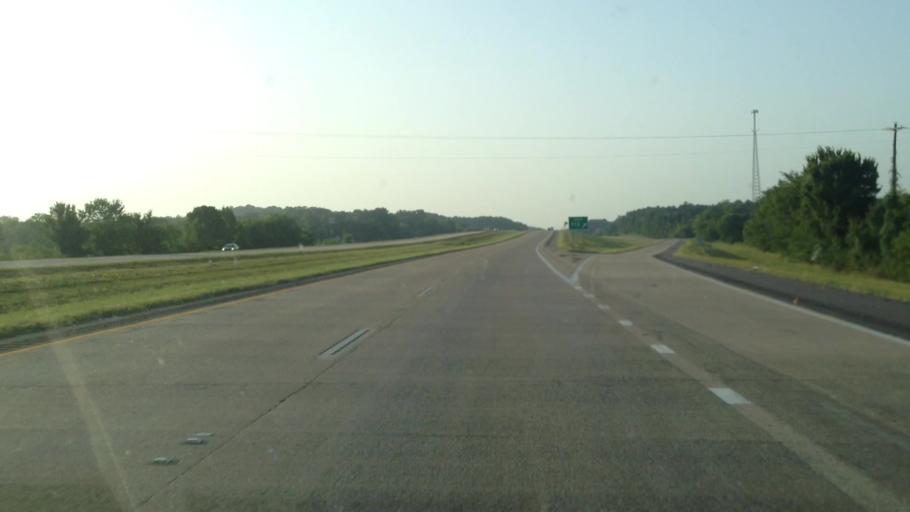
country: US
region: Louisiana
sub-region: Grant Parish
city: Colfax
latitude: 31.4981
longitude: -92.8667
